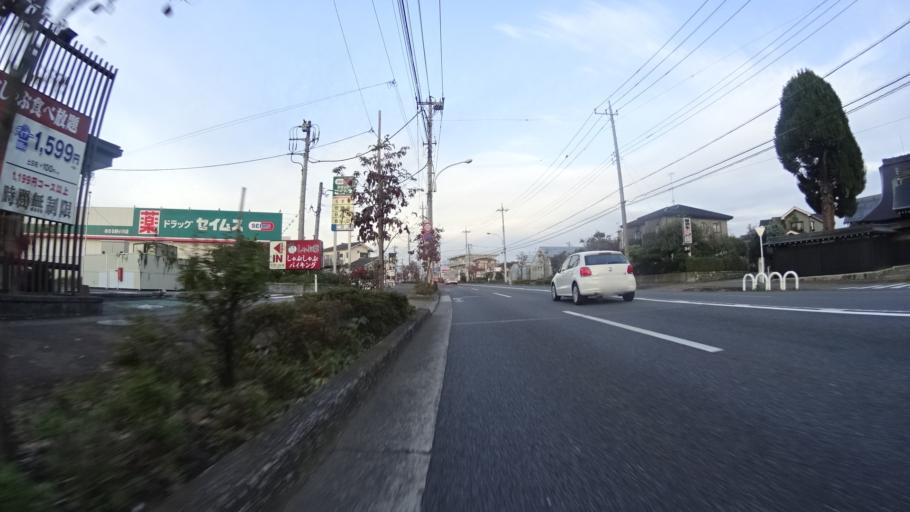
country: JP
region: Tokyo
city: Fussa
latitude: 35.7216
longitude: 139.3142
